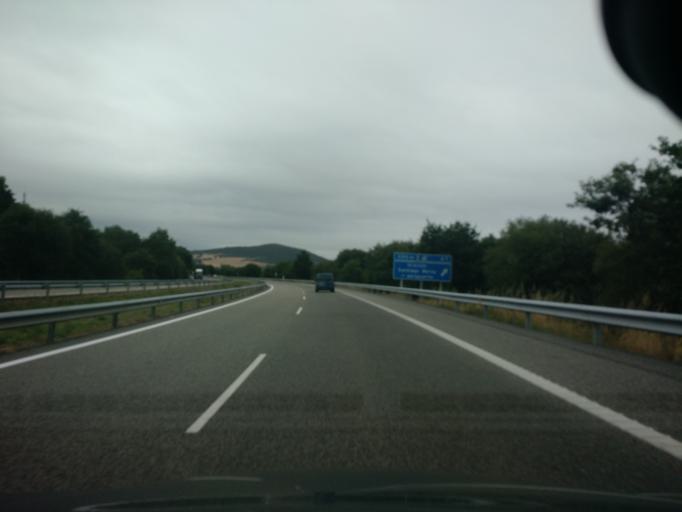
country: ES
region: Galicia
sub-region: Provincia da Coruna
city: Santiago de Compostela
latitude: 42.8981
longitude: -8.5029
